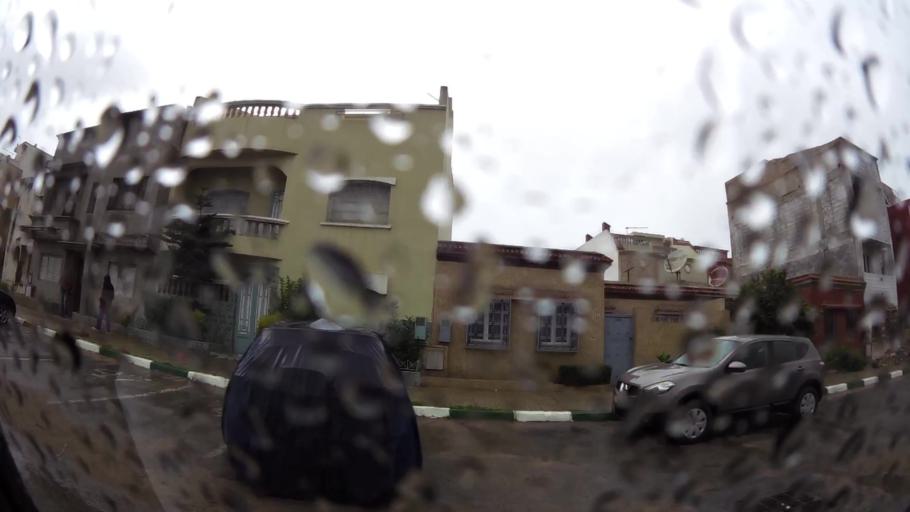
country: MA
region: Grand Casablanca
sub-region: Mediouna
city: Tit Mellil
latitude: 33.6186
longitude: -7.4795
